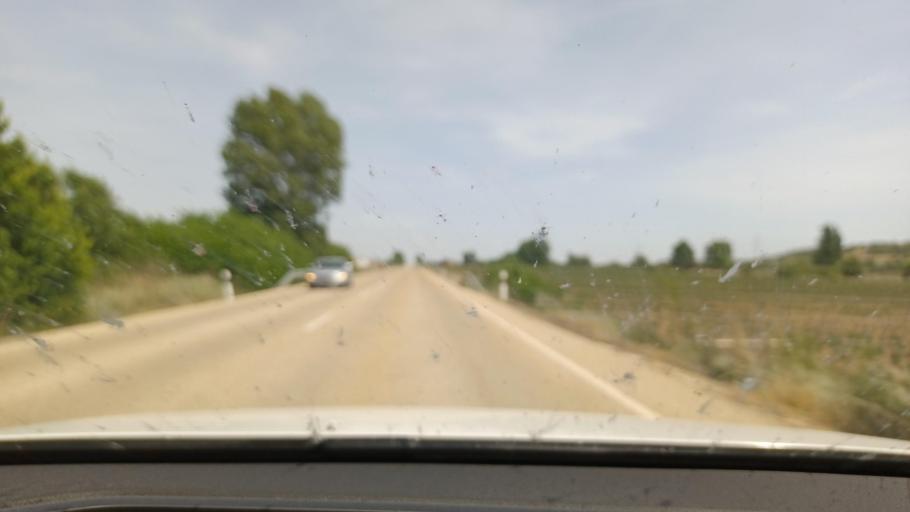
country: ES
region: Castille and Leon
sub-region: Provincia de Soria
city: Centenera de Andaluz
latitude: 41.4789
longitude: -2.7375
